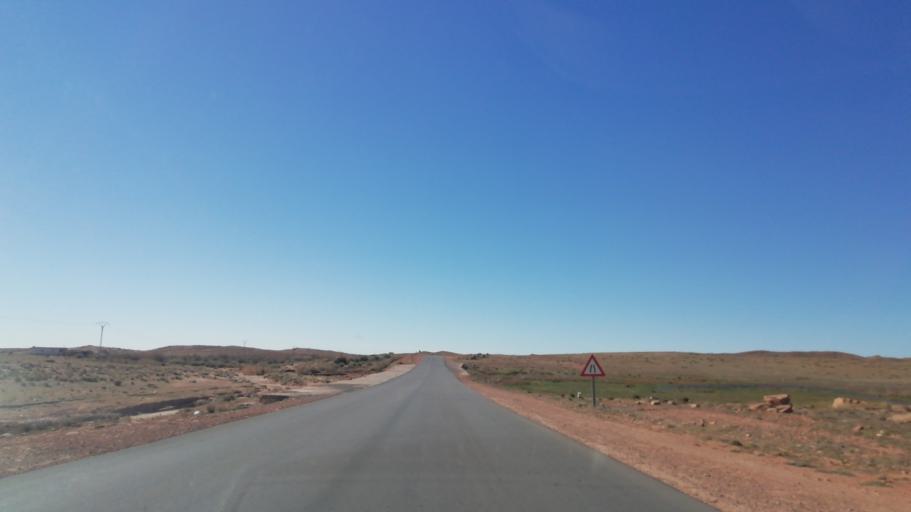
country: DZ
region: El Bayadh
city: El Bayadh
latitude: 33.6438
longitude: 1.3925
